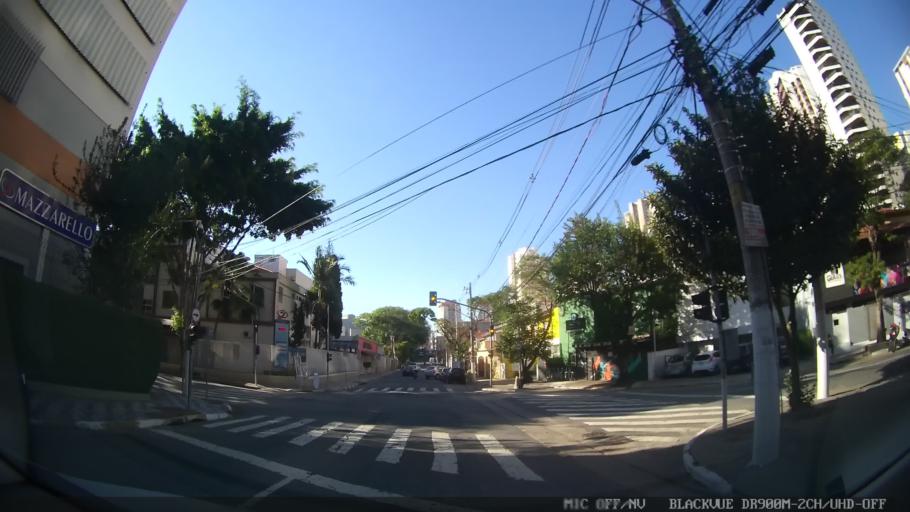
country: BR
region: Sao Paulo
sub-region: Sao Paulo
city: Sao Paulo
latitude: -23.4917
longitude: -46.6326
